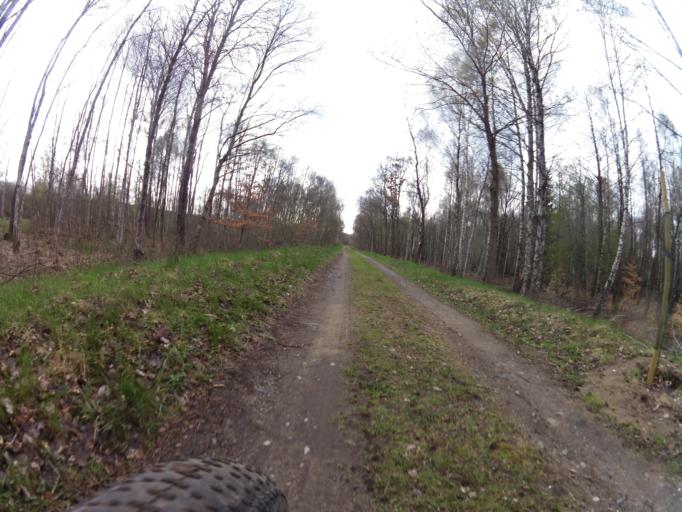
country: PL
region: West Pomeranian Voivodeship
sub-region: Powiat slawienski
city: Slawno
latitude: 54.3302
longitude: 16.7336
